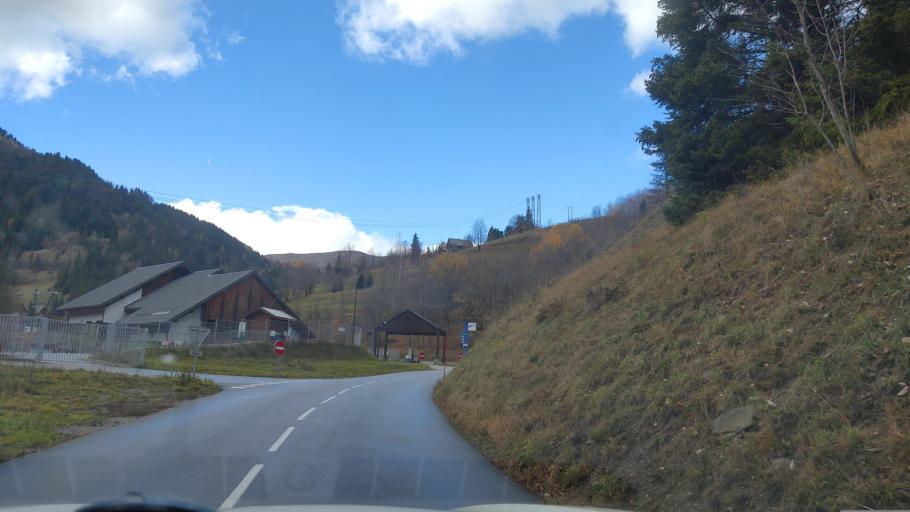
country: FR
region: Rhone-Alpes
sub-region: Departement de la Savoie
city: Saint-Jean-de-Maurienne
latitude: 45.1924
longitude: 6.2920
